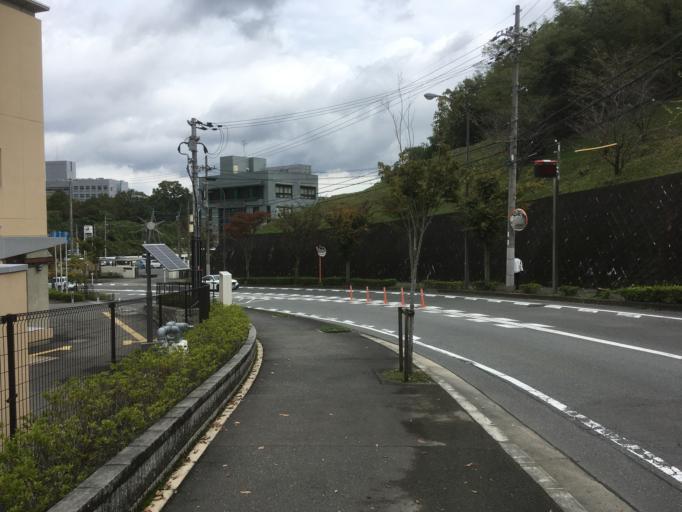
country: JP
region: Nara
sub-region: Ikoma-shi
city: Ikoma
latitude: 34.7290
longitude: 135.7304
